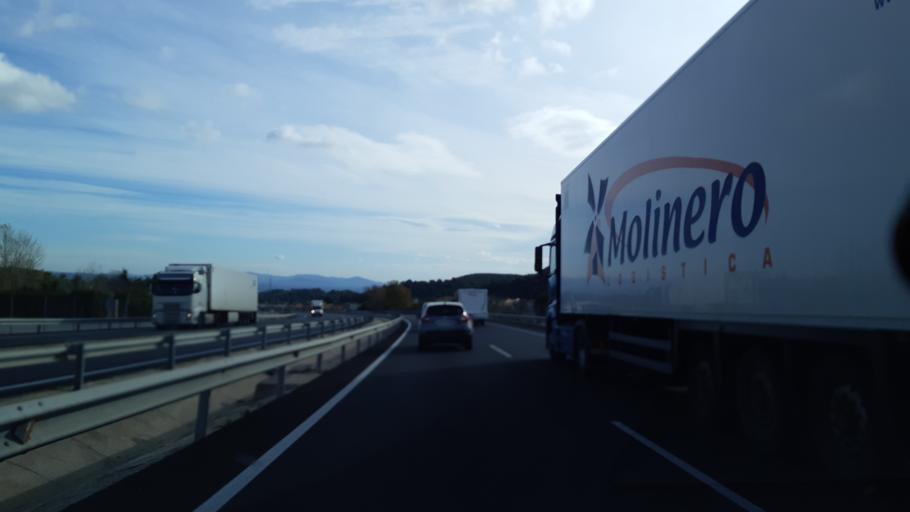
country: ES
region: Catalonia
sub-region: Provincia de Barcelona
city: Collbato
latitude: 41.5647
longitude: 1.8118
